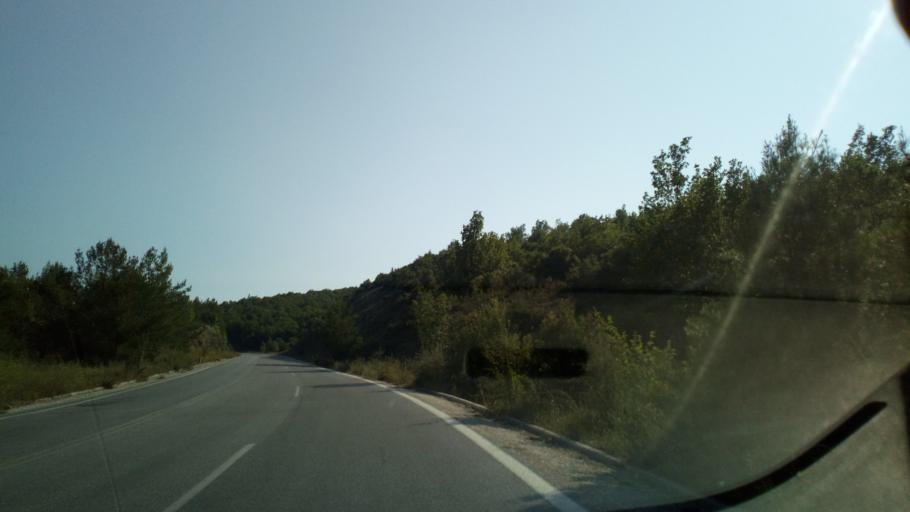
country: GR
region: Central Macedonia
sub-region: Nomos Chalkidikis
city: Polygyros
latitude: 40.4226
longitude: 23.4215
